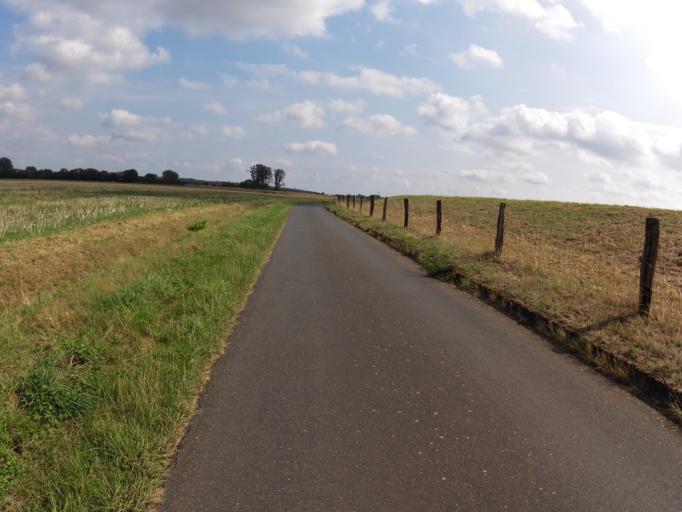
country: DE
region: Lower Saxony
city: Hoya
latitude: 52.8150
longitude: 9.1632
